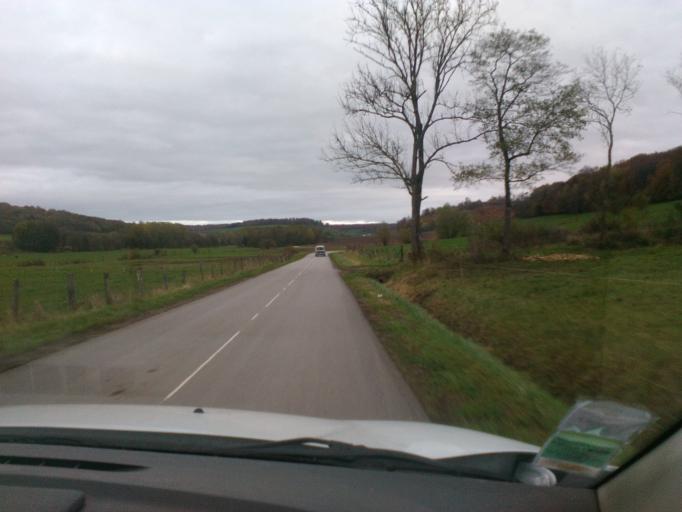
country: FR
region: Lorraine
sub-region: Departement des Vosges
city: Mirecourt
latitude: 48.2749
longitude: 6.2356
